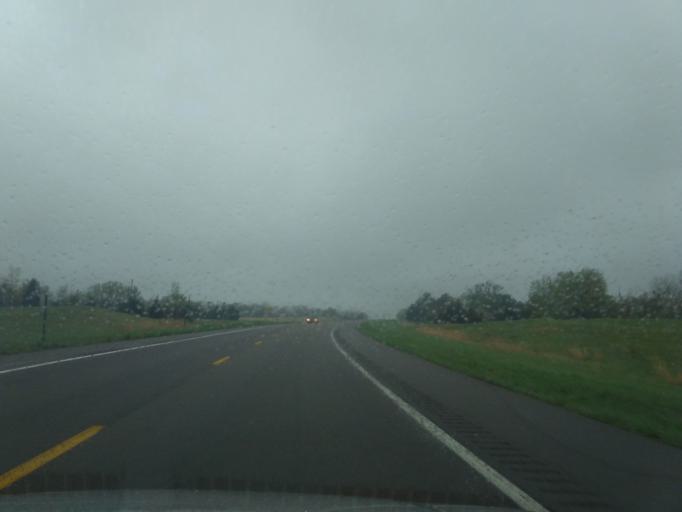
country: US
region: Nebraska
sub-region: Madison County
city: Norfolk
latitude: 42.0779
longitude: -97.3278
